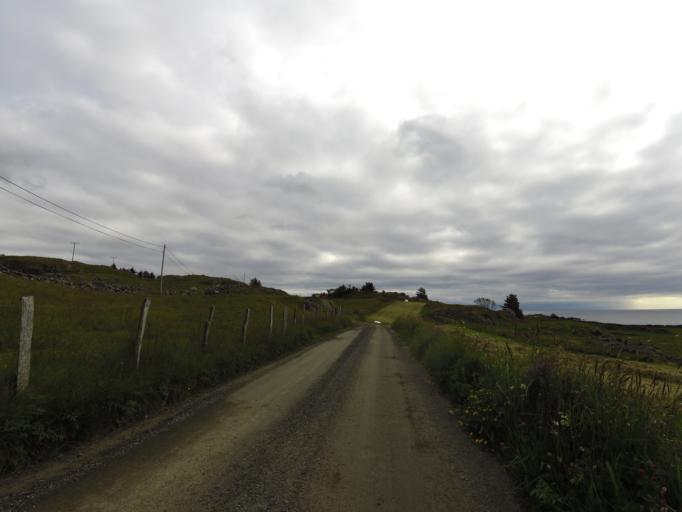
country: NO
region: Vest-Agder
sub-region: Farsund
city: Vestbygd
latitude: 58.1425
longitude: 6.6118
